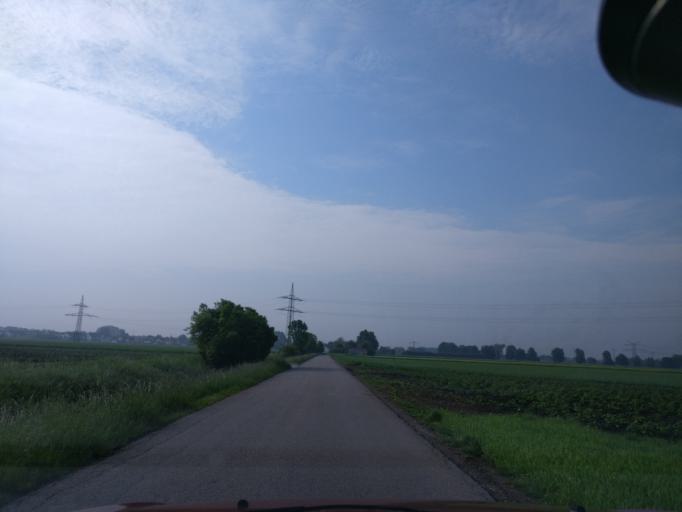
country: DE
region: Bavaria
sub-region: Upper Bavaria
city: Karlsfeld
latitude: 48.2167
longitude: 11.4435
